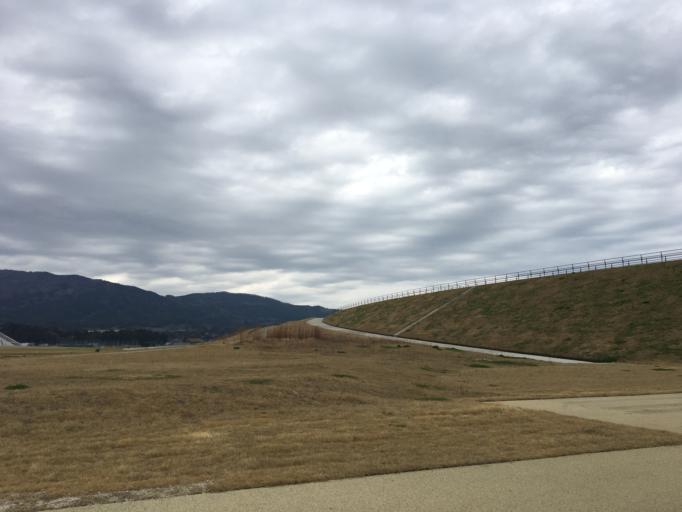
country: JP
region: Iwate
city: Ofunato
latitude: 39.0033
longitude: 141.6258
